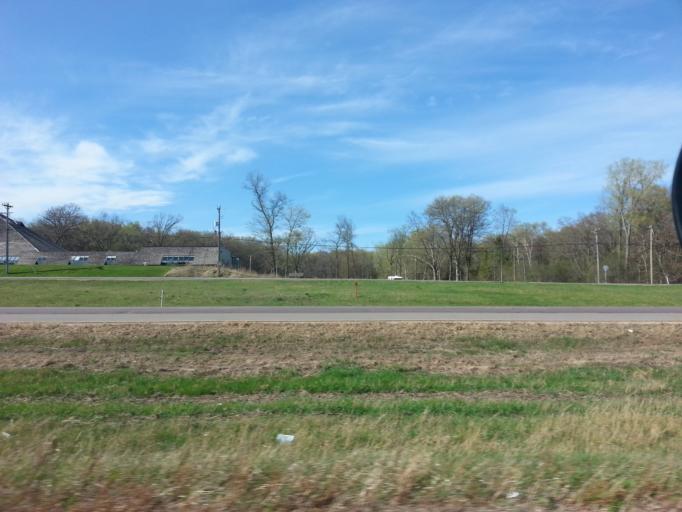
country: US
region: Minnesota
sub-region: Washington County
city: Mahtomedi
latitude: 45.0355
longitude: -92.9219
